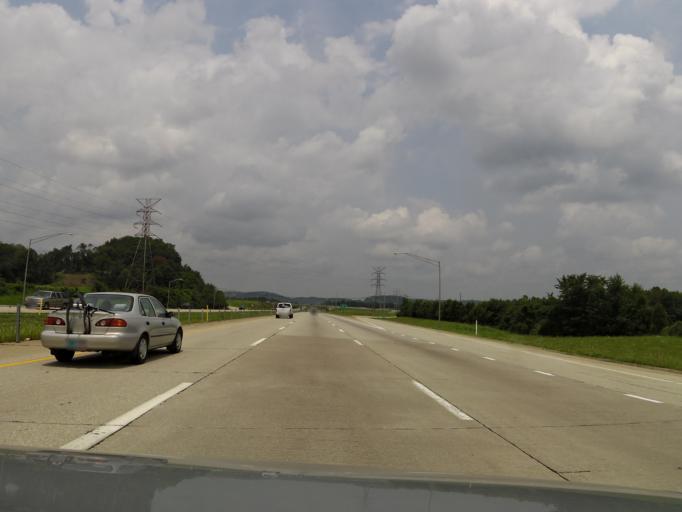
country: US
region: Kentucky
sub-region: Bullitt County
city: Shepherdsville
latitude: 37.9198
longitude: -85.6871
